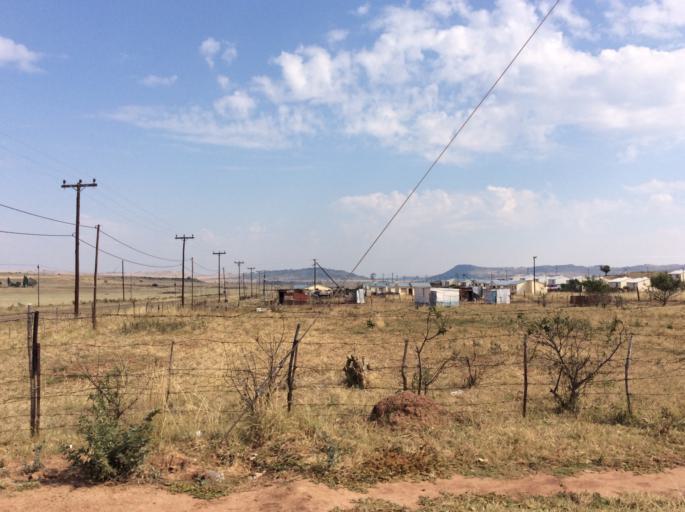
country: LS
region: Mafeteng
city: Mafeteng
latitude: -29.9892
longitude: 27.0037
